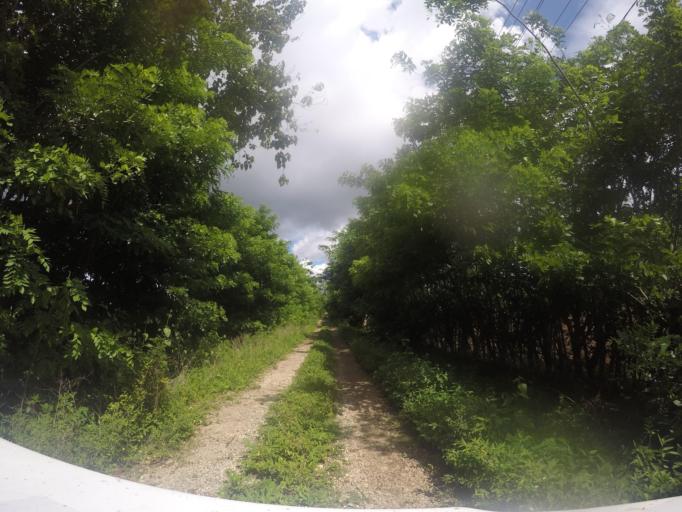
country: TL
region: Lautem
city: Lospalos
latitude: -8.4941
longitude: 127.0067
